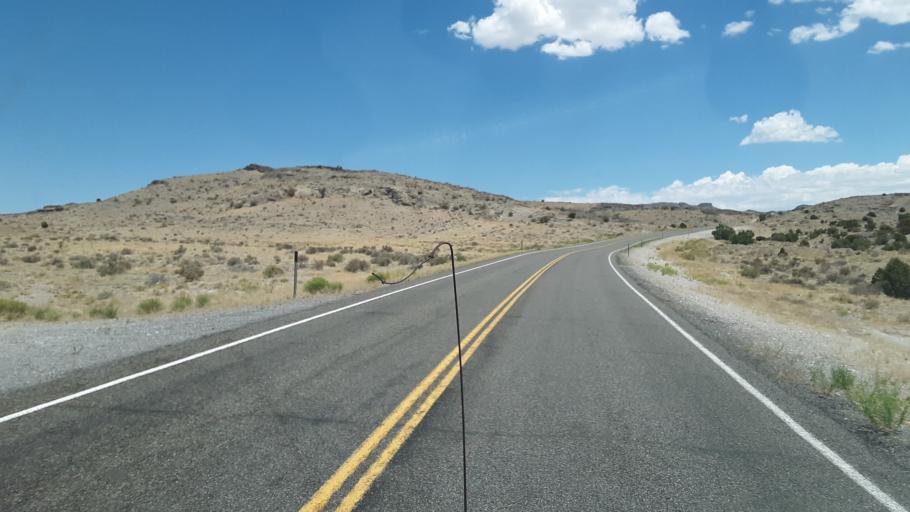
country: US
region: Utah
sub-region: Beaver County
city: Milford
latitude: 39.0789
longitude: -113.7028
